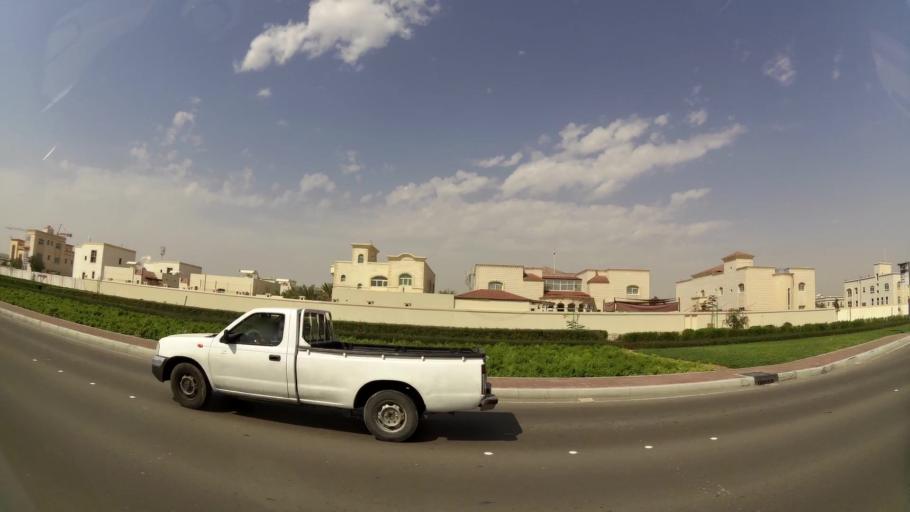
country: AE
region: Abu Dhabi
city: Abu Dhabi
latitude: 24.3256
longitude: 54.5590
